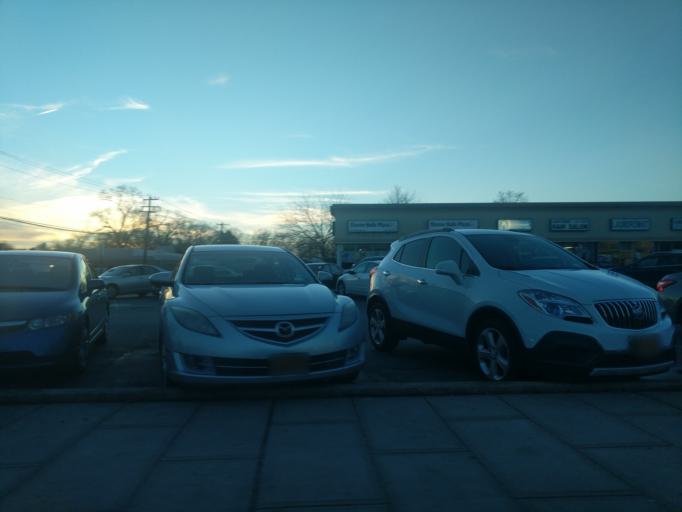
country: US
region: New York
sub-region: Nassau County
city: Wantagh
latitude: 40.6738
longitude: -73.5102
